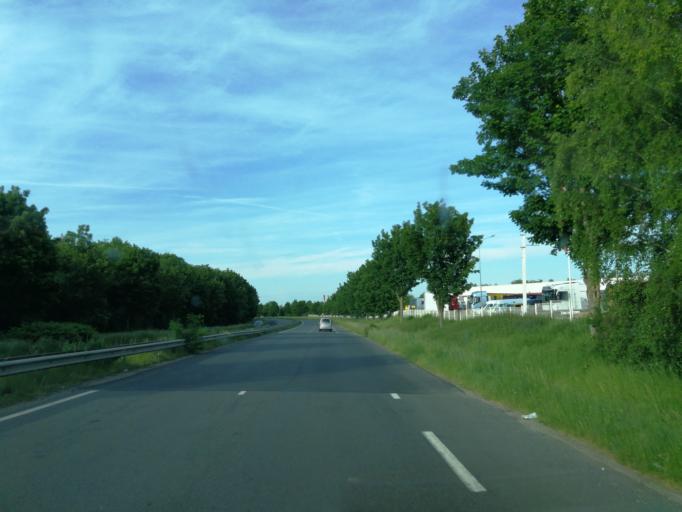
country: FR
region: Centre
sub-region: Departement d'Eure-et-Loir
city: Gasville-Oiseme
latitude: 48.4419
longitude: 1.5248
